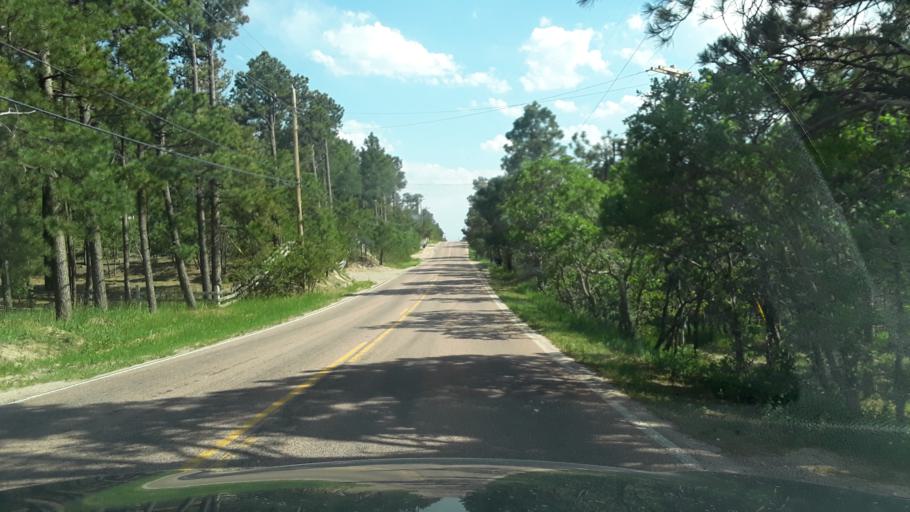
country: US
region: Colorado
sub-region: El Paso County
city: Gleneagle
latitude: 39.0460
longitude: -104.7849
